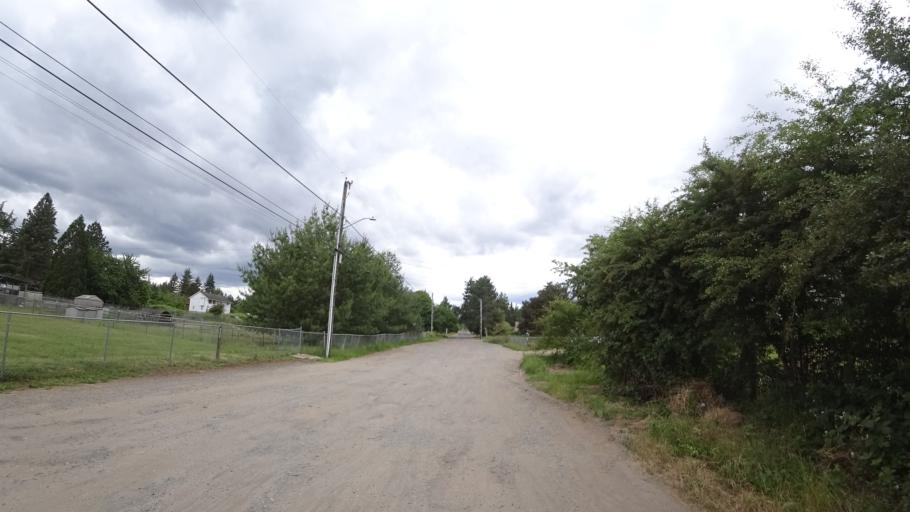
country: US
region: Oregon
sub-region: Multnomah County
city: Lents
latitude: 45.4880
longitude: -122.5287
